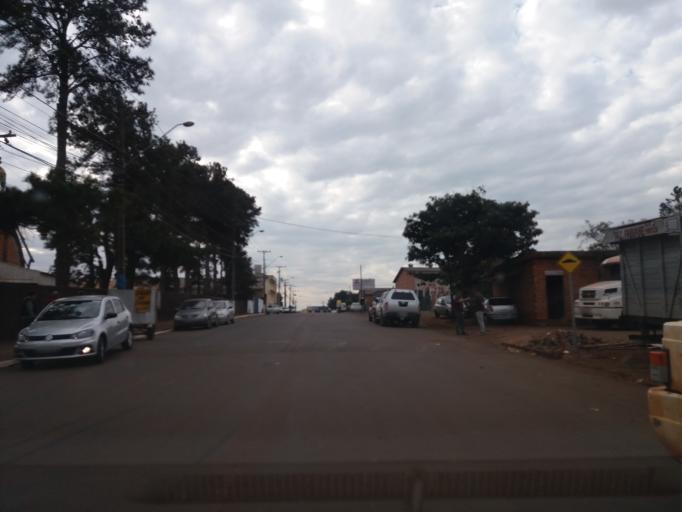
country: BR
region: Parana
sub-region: Cascavel
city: Cascavel
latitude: -24.9838
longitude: -53.4642
